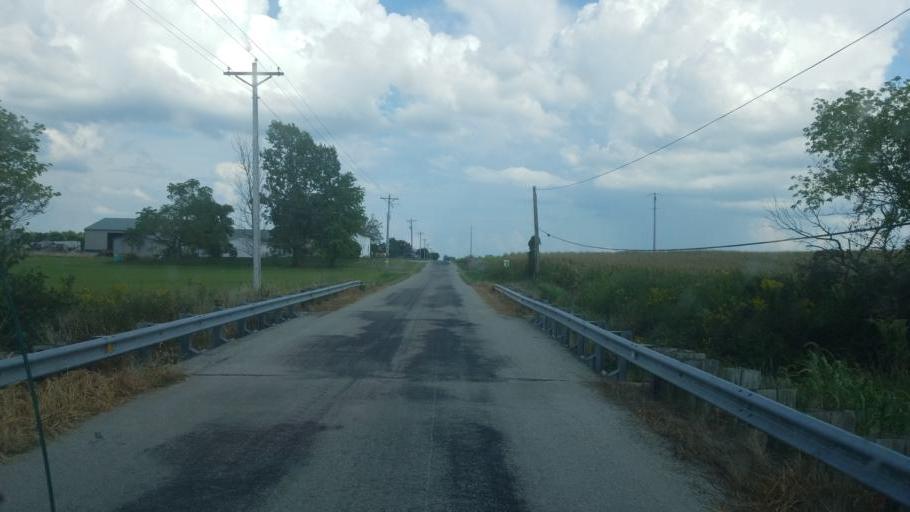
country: US
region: Ohio
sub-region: Huron County
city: Willard
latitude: 40.9968
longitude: -82.8428
